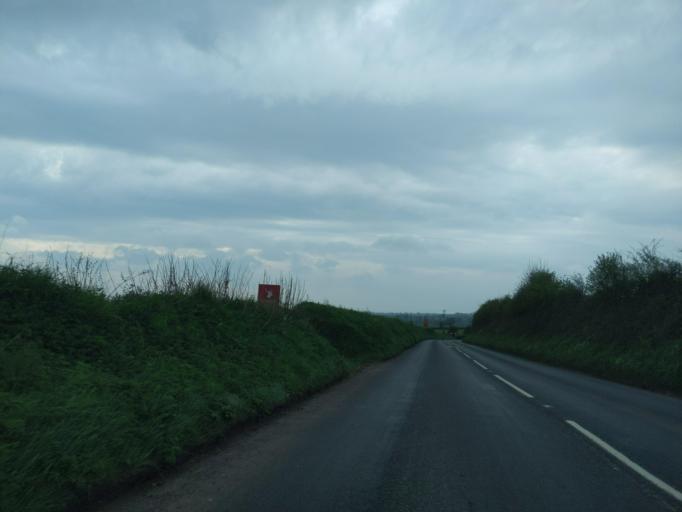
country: GB
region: England
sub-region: Devon
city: Crediton
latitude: 50.8043
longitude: -3.7250
